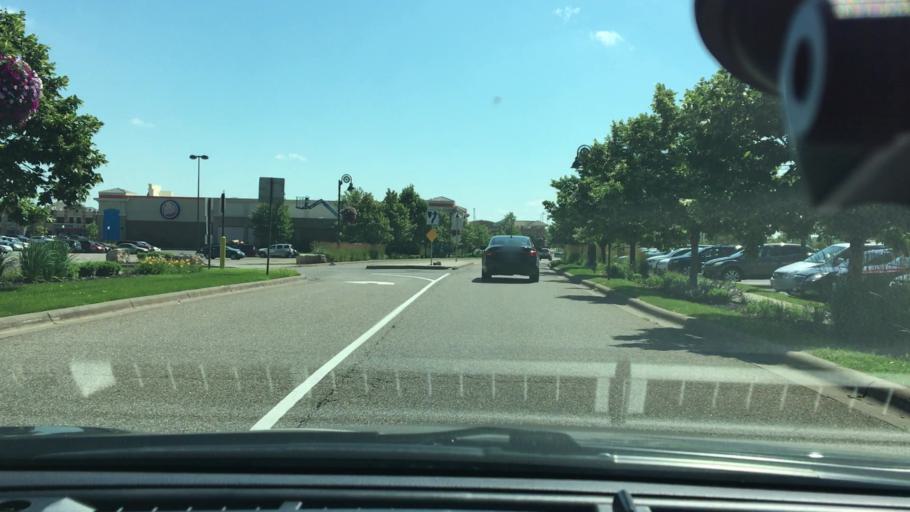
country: US
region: Minnesota
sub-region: Hennepin County
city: Maple Grove
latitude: 45.0929
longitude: -93.4309
